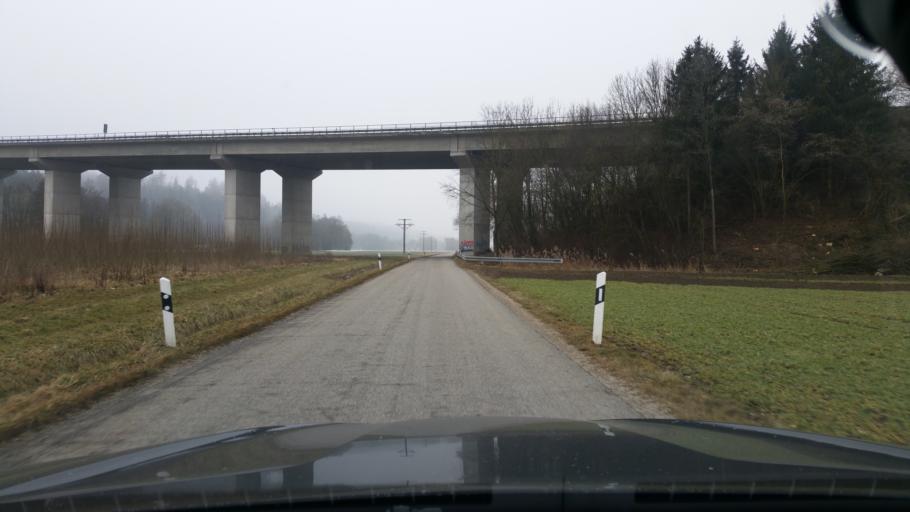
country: DE
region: Bavaria
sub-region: Lower Bavaria
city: Weihmichl
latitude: 48.5644
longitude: 12.0904
